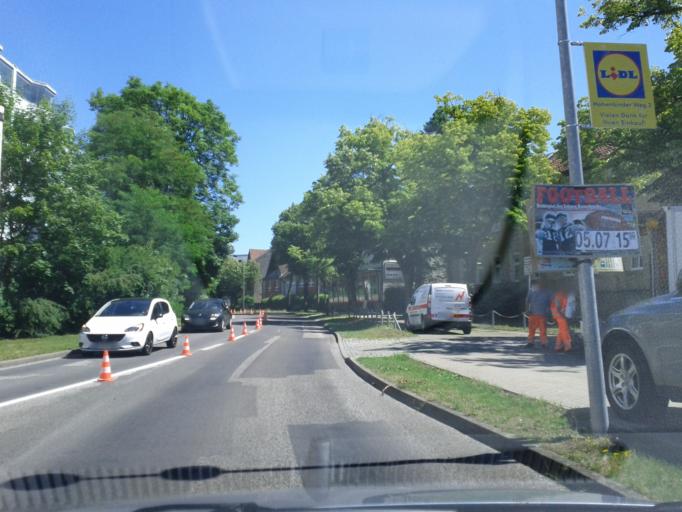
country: DE
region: Brandenburg
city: Erkner
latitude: 52.4197
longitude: 13.7548
